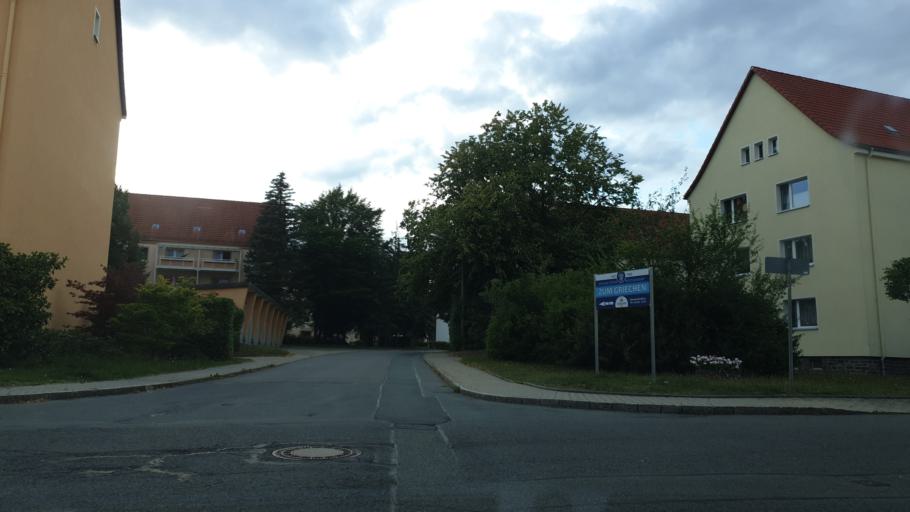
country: DE
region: Saxony
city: Stollberg
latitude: 50.7141
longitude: 12.7777
